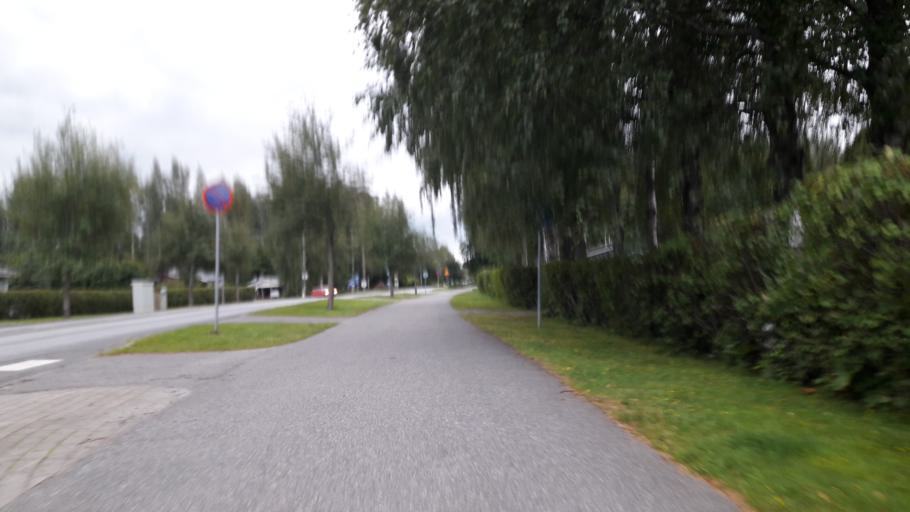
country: FI
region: North Karelia
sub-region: Joensuu
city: Joensuu
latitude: 62.6091
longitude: 29.7380
